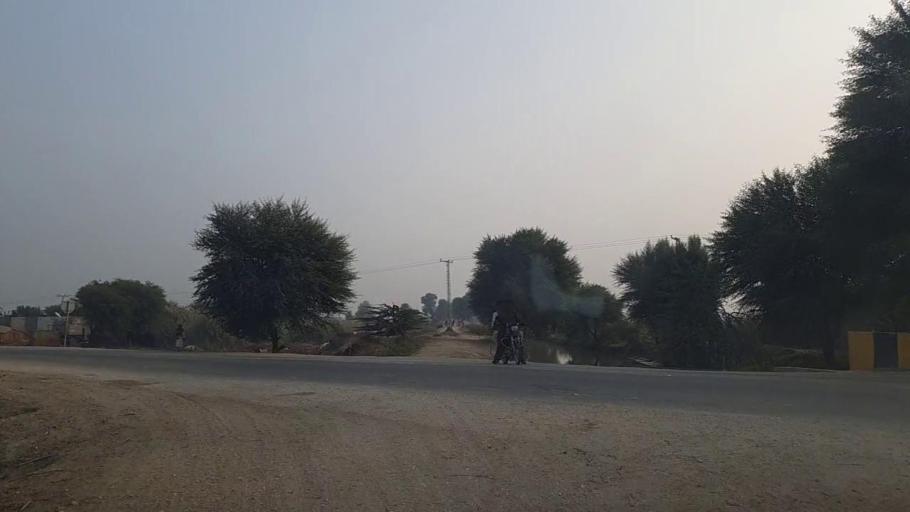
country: PK
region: Sindh
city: Sinjhoro
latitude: 26.1157
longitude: 68.8046
